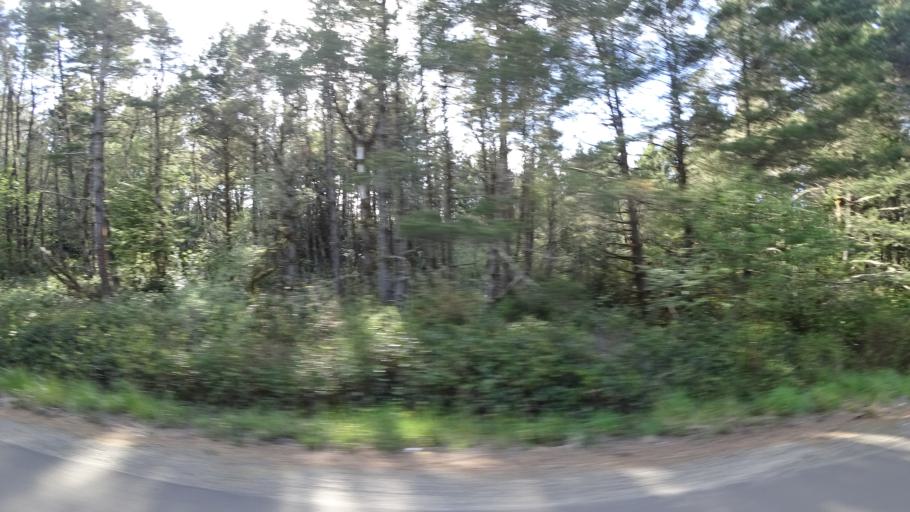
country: US
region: Oregon
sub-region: Lane County
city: Dunes City
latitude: 43.8899
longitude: -124.1197
